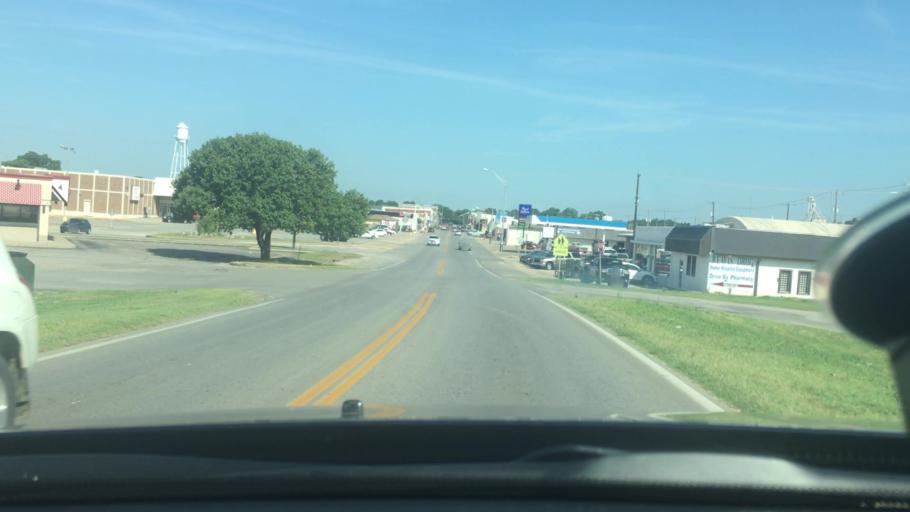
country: US
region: Oklahoma
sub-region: Garvin County
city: Pauls Valley
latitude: 34.7365
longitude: -97.2151
